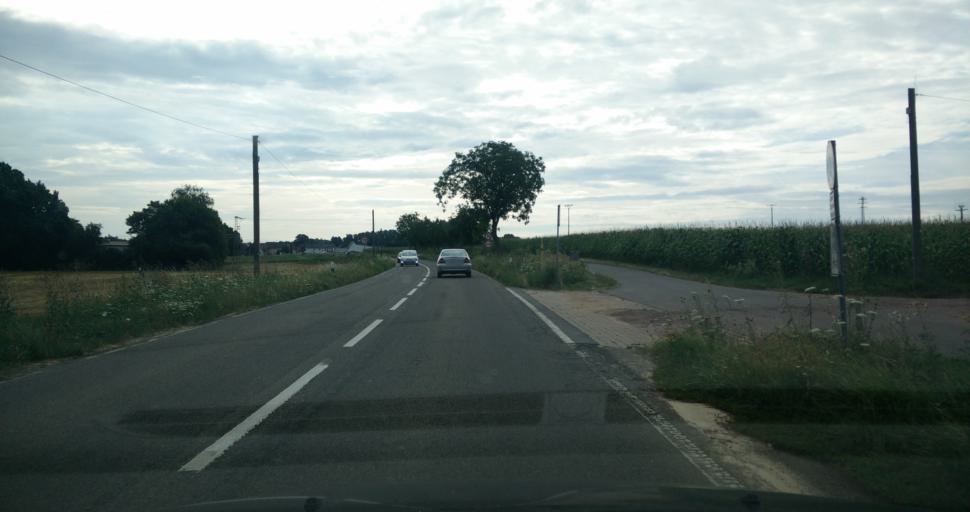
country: DE
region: Rheinland-Pfalz
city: Barbelroth
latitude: 49.0963
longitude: 8.0796
